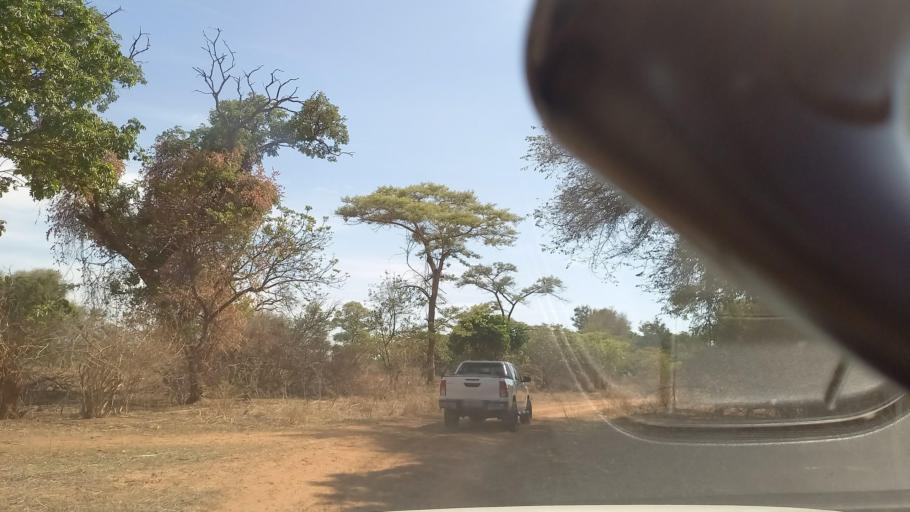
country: ZM
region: Southern
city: Mazabuka
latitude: -16.0326
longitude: 27.6241
